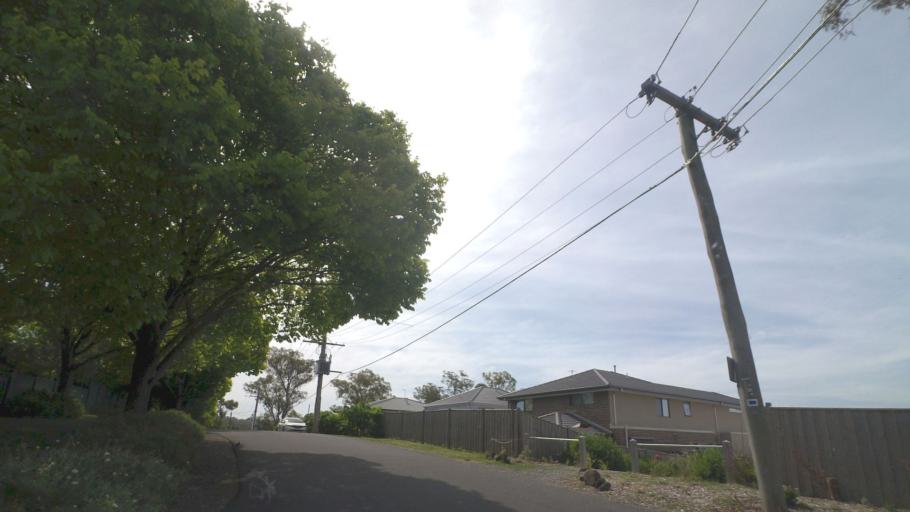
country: AU
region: Victoria
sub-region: Maroondah
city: Croydon North
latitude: -37.7813
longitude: 145.2946
